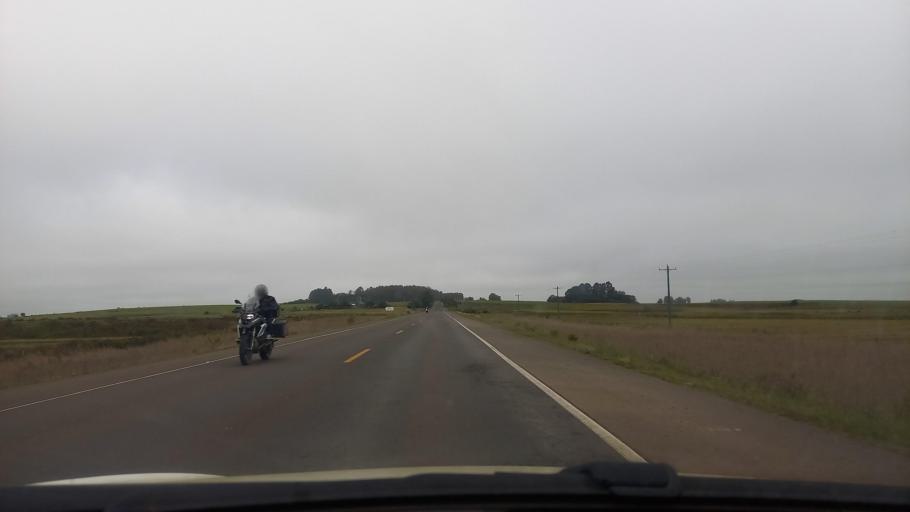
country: BR
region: Rio Grande do Sul
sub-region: Rosario Do Sul
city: Rosario do Sul
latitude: -30.3160
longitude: -54.9987
